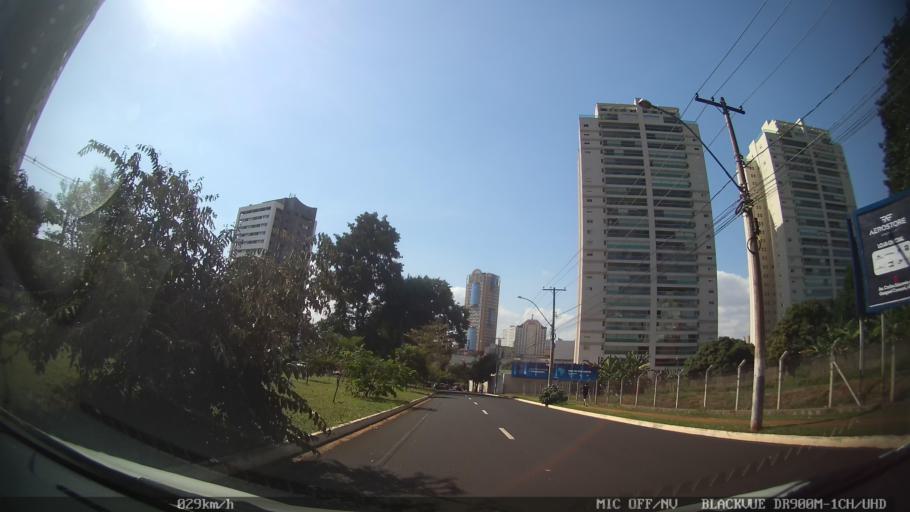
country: BR
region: Sao Paulo
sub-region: Ribeirao Preto
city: Ribeirao Preto
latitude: -21.2151
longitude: -47.8211
